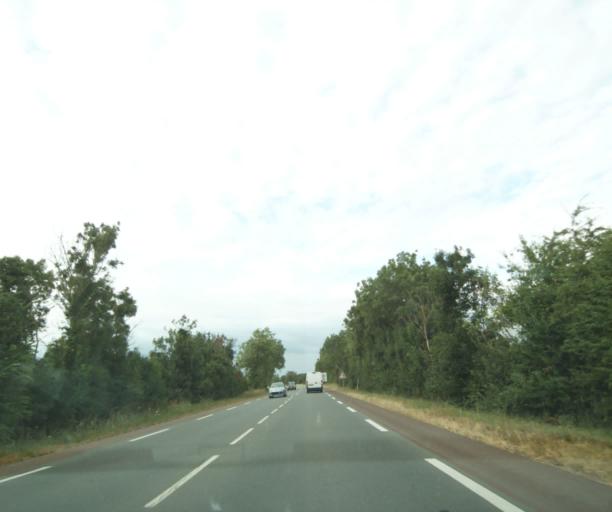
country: FR
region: Poitou-Charentes
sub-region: Departement de la Charente-Maritime
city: Marans
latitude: 46.2823
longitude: -0.9952
